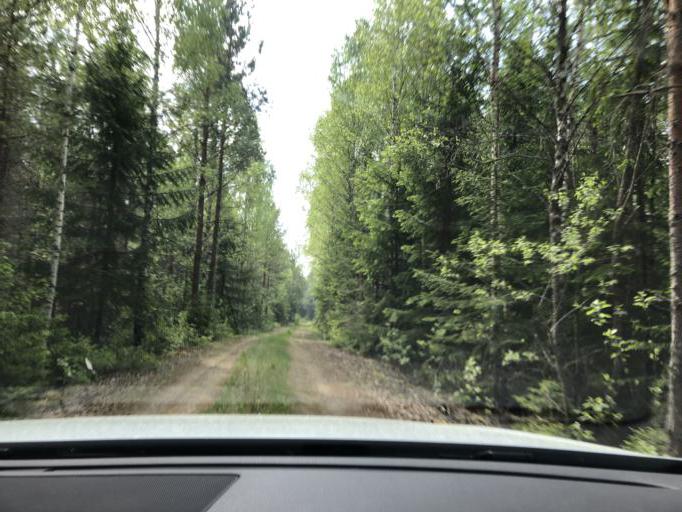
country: SE
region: Dalarna
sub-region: Avesta Kommun
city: Horndal
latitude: 60.2225
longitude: 16.5162
